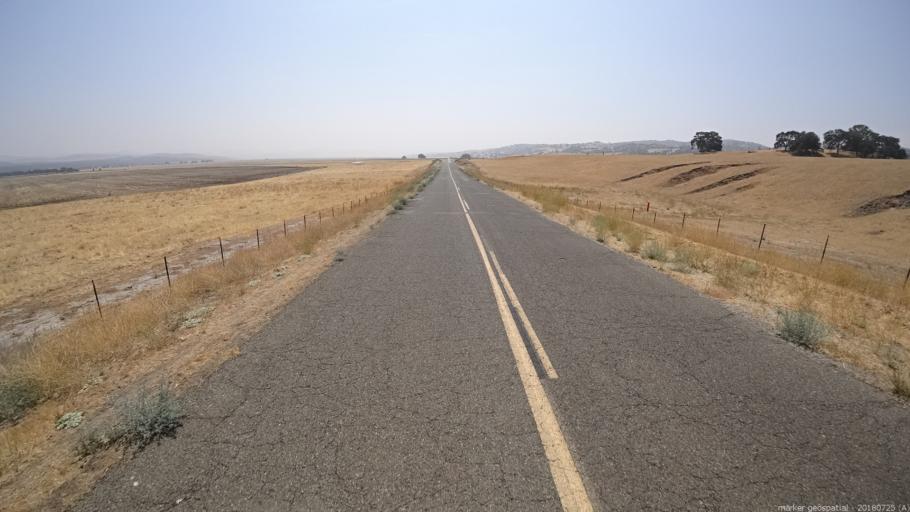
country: US
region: California
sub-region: San Luis Obispo County
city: Shandon
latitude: 35.8065
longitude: -120.3688
